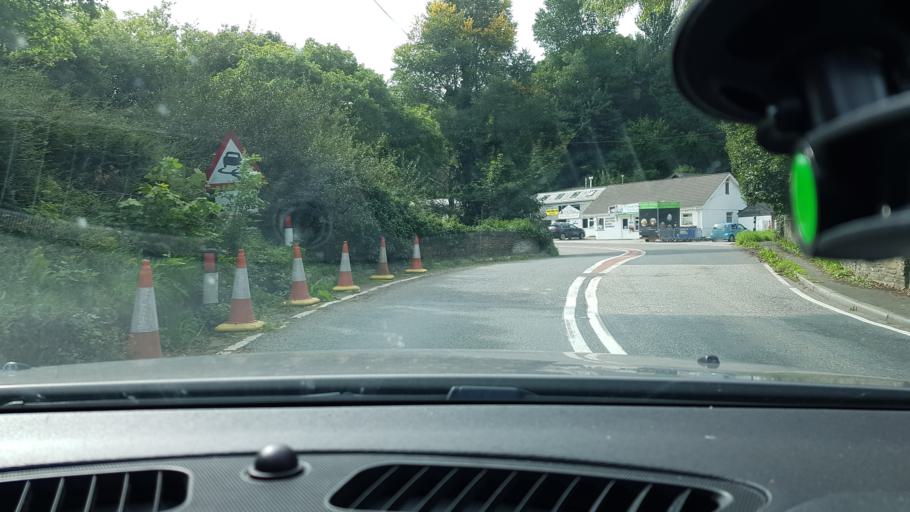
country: GB
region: England
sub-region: Cornwall
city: Camelford
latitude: 50.5933
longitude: -4.7258
